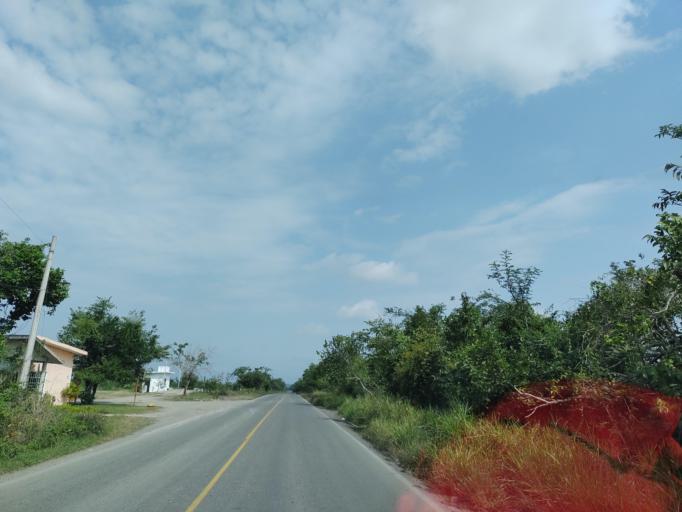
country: MX
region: Puebla
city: Espinal
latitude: 20.2804
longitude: -97.3309
